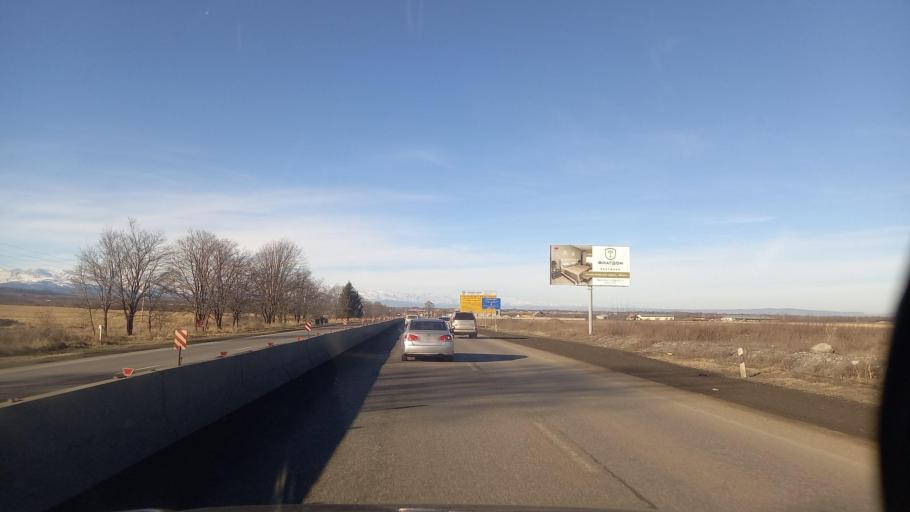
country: RU
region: North Ossetia
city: Vladikavkaz
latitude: 43.0256
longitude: 44.6246
